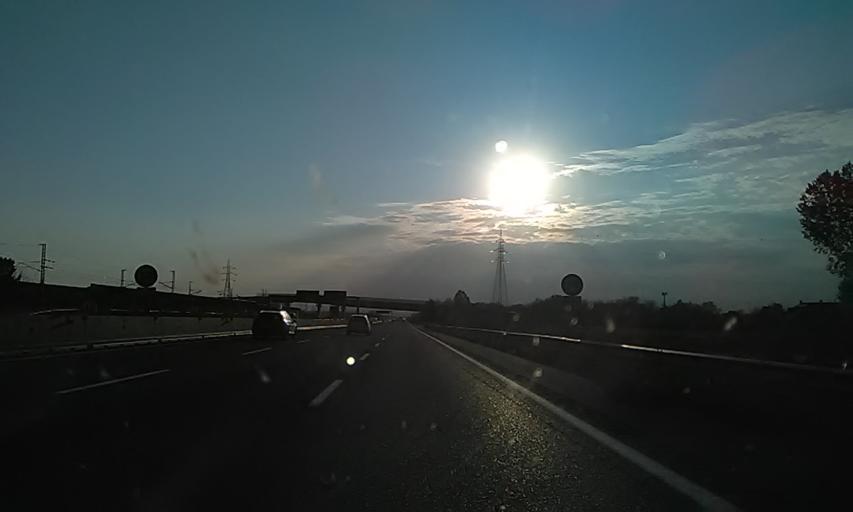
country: IT
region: Piedmont
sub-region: Provincia di Novara
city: Recetto
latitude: 45.4645
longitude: 8.4348
